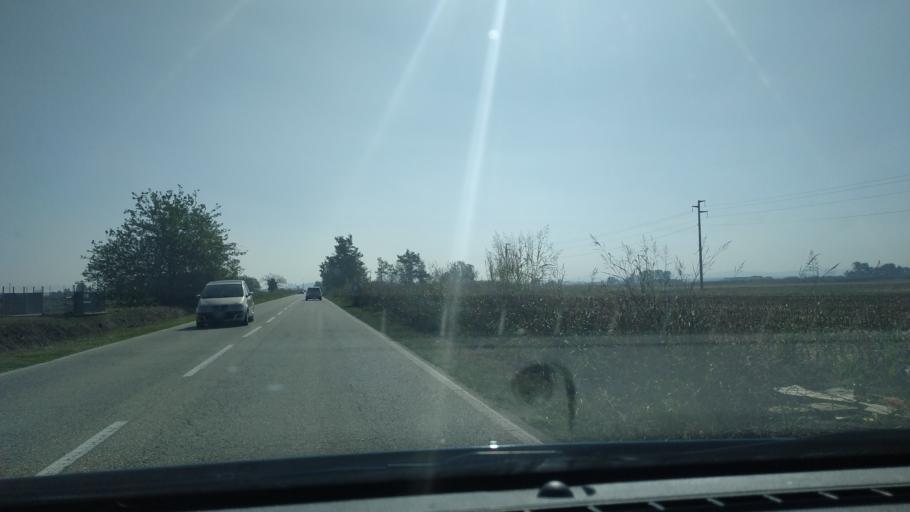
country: IT
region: Piedmont
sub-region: Provincia di Alessandria
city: Ticineto
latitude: 45.0935
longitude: 8.5404
